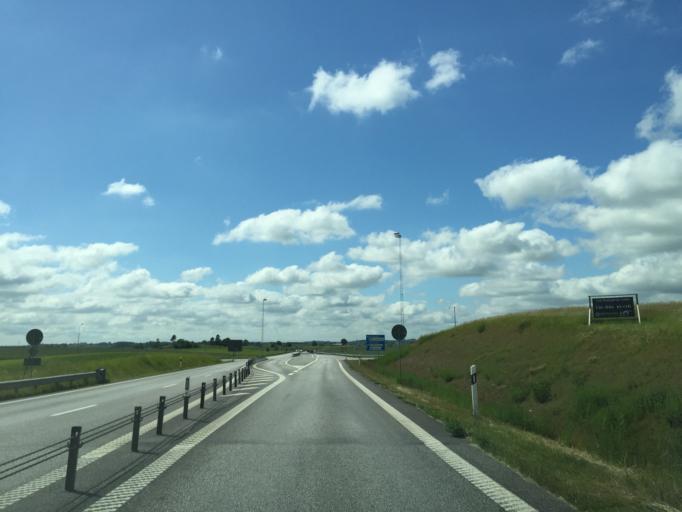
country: SE
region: Skane
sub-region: Skurups Kommun
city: Rydsgard
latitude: 55.4828
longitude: 13.5951
